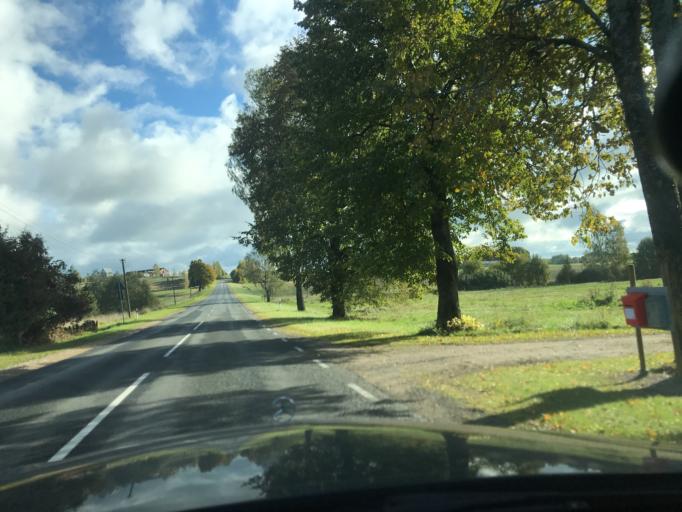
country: EE
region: Tartu
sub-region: Elva linn
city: Elva
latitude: 58.0092
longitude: 26.2330
